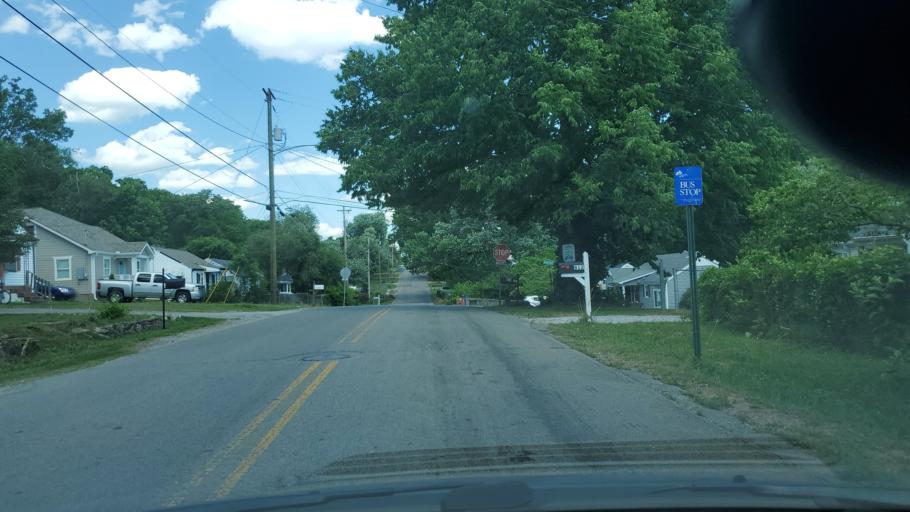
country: US
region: Tennessee
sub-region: Davidson County
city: Nashville
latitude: 36.2004
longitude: -86.7547
